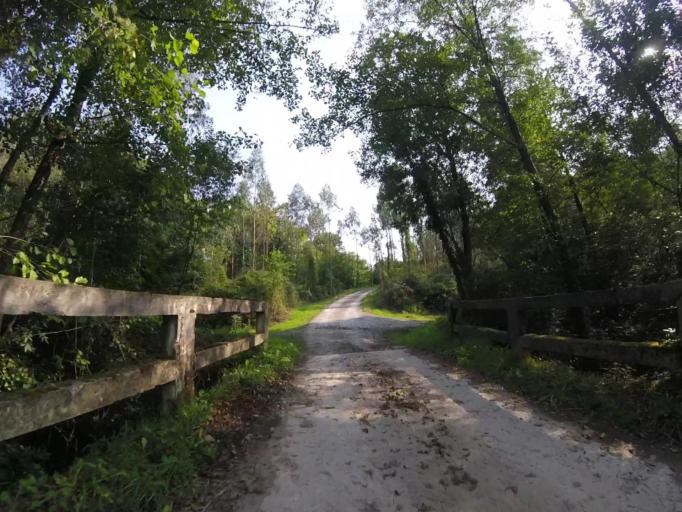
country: ES
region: Basque Country
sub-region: Provincia de Guipuzcoa
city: Astigarraga
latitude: 43.2353
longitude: -1.9340
